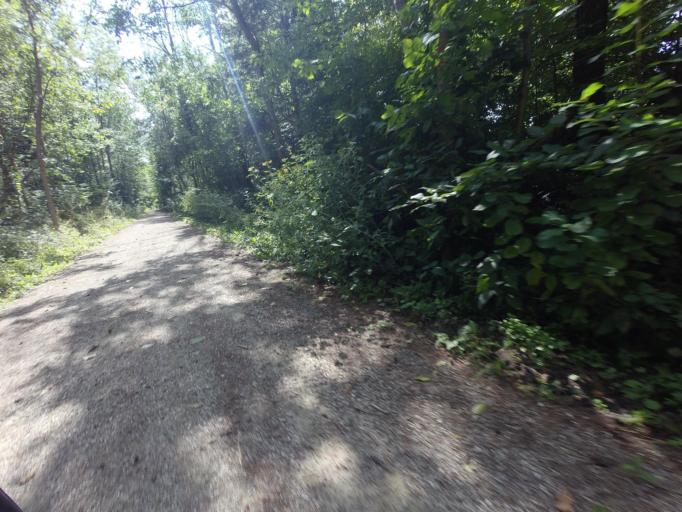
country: CA
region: Ontario
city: Huron East
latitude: 43.7050
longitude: -81.3597
